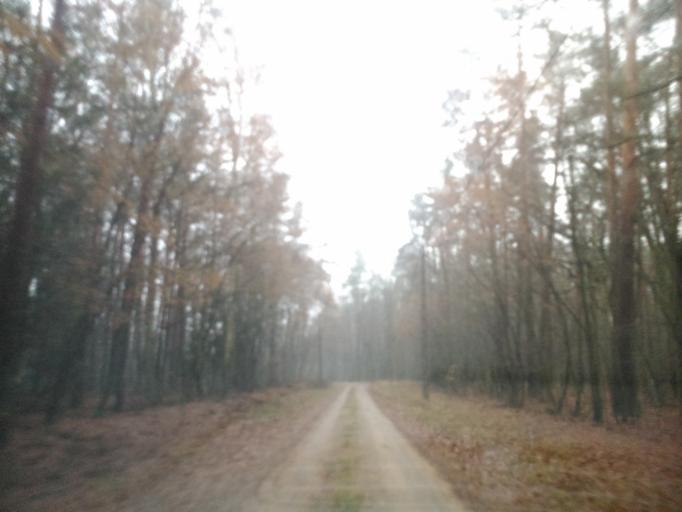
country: PL
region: Kujawsko-Pomorskie
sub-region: Powiat golubsko-dobrzynski
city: Golub-Dobrzyn
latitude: 53.1447
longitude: 19.1293
